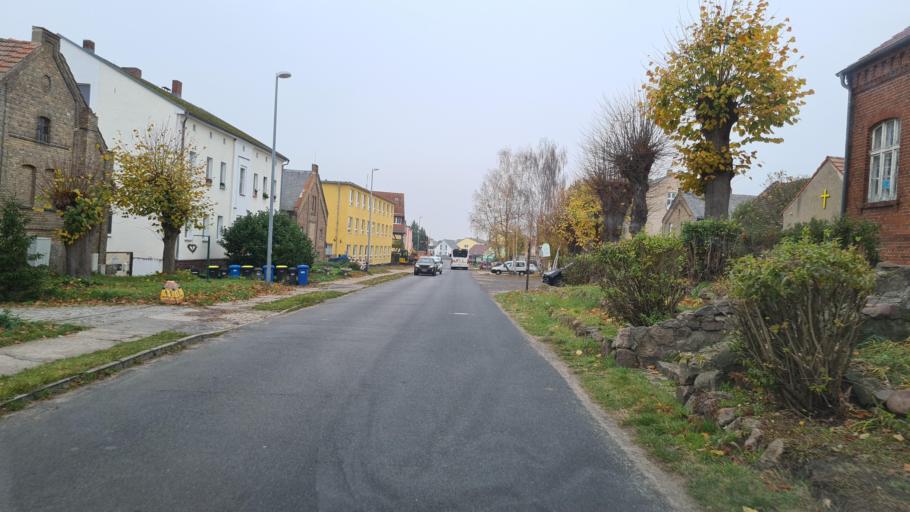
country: DE
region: Brandenburg
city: Roskow
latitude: 52.4186
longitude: 12.7194
